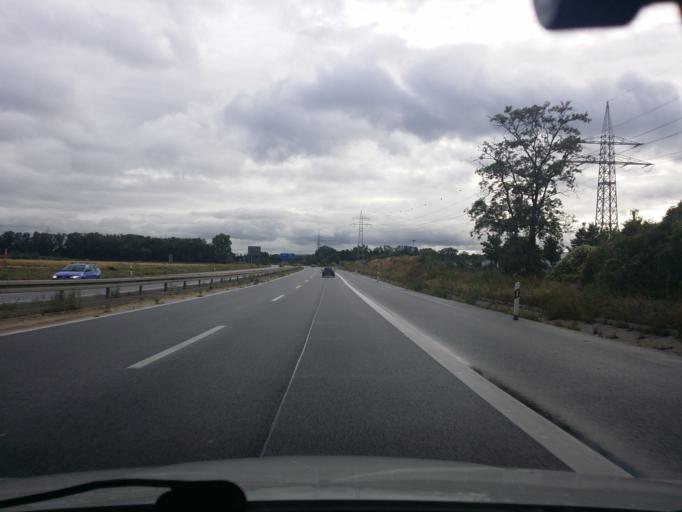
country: DE
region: Hesse
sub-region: Regierungsbezirk Darmstadt
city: Ginsheim-Gustavsburg
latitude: 49.9933
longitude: 8.3432
